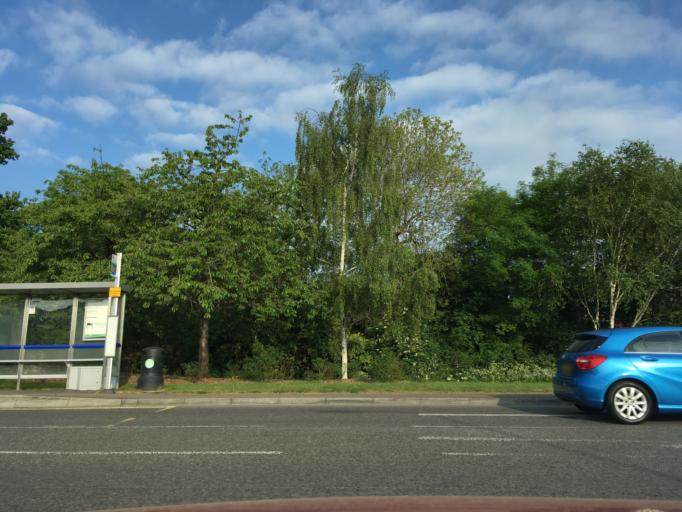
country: GB
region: England
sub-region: South Gloucestershire
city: Almondsbury
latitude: 51.5408
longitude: -2.5600
